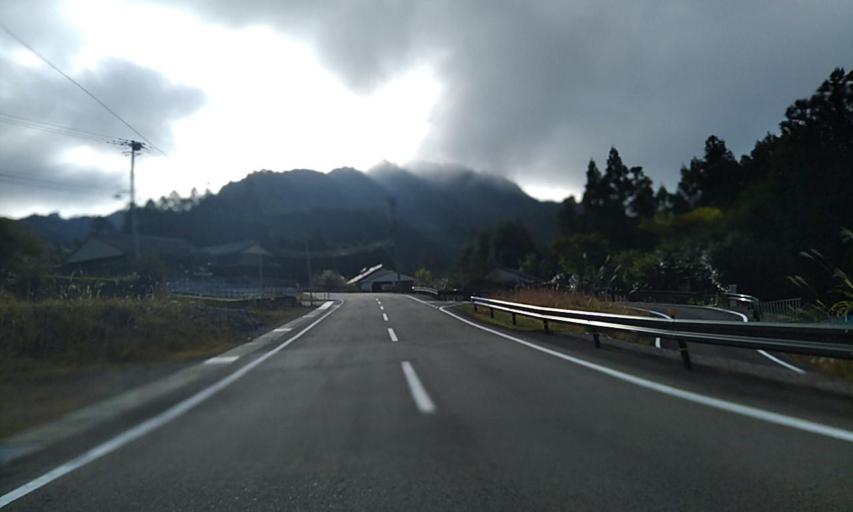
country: JP
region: Wakayama
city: Shingu
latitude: 33.8766
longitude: 135.8654
